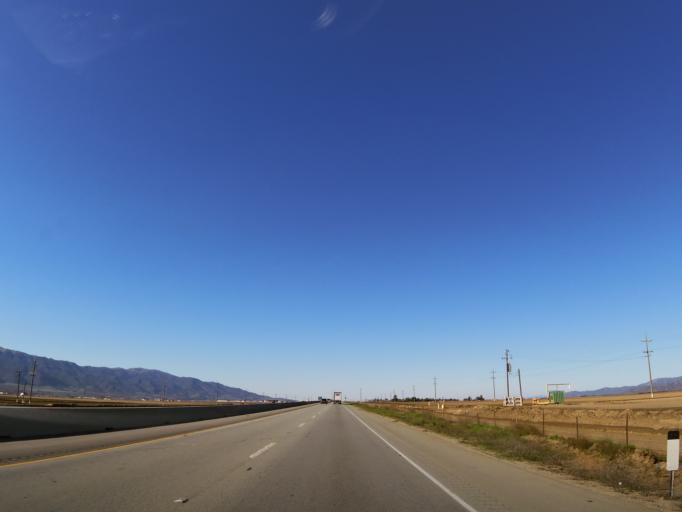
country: US
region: California
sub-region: Monterey County
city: Gonzales
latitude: 36.4780
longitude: -121.4086
